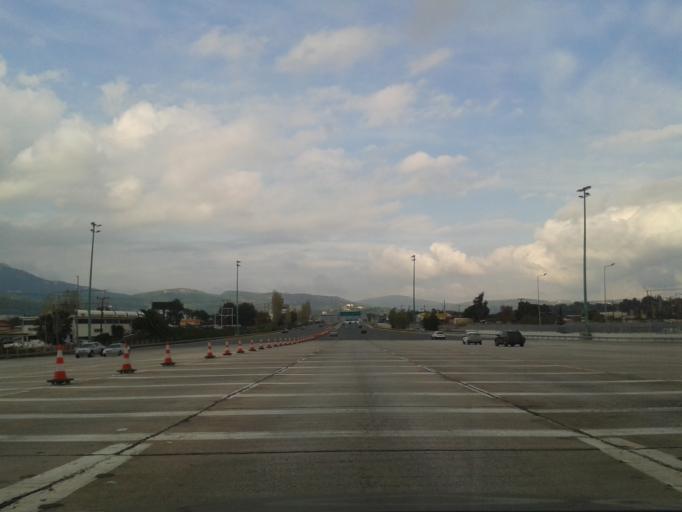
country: GR
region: Attica
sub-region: Nomarchia Anatolikis Attikis
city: Agios Stefanos
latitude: 38.1766
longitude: 23.8542
